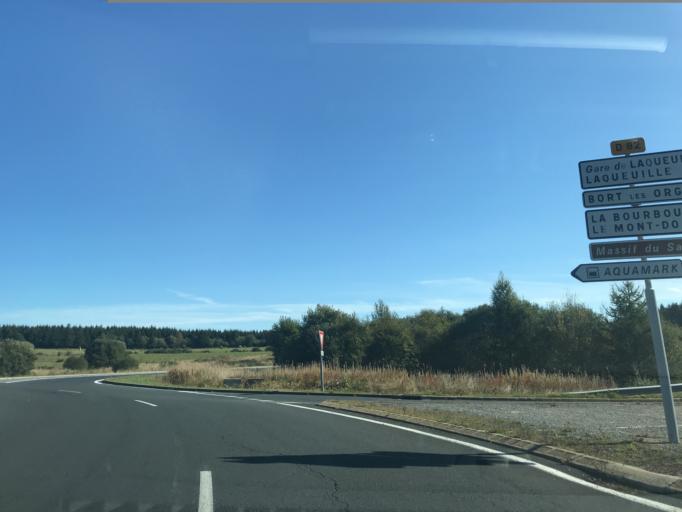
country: FR
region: Auvergne
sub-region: Departement du Puy-de-Dome
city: Saint-Sauves-d'Auvergne
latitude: 45.6552
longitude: 2.6901
